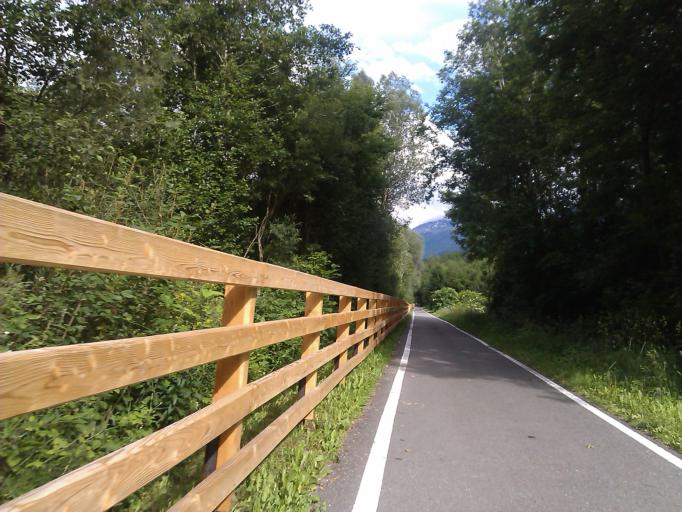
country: IT
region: Trentino-Alto Adige
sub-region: Bolzano
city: Sluderno
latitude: 46.6452
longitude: 10.5808
